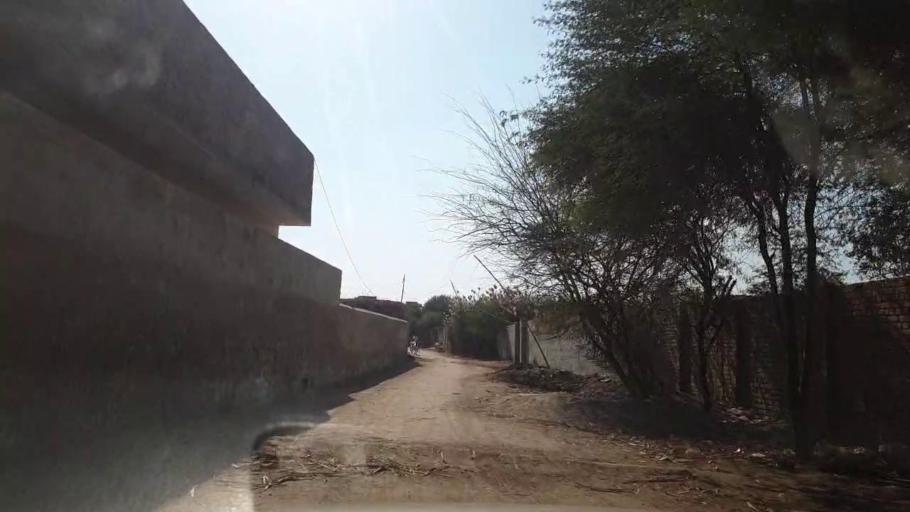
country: PK
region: Sindh
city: Tando Allahyar
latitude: 25.4828
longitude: 68.6784
